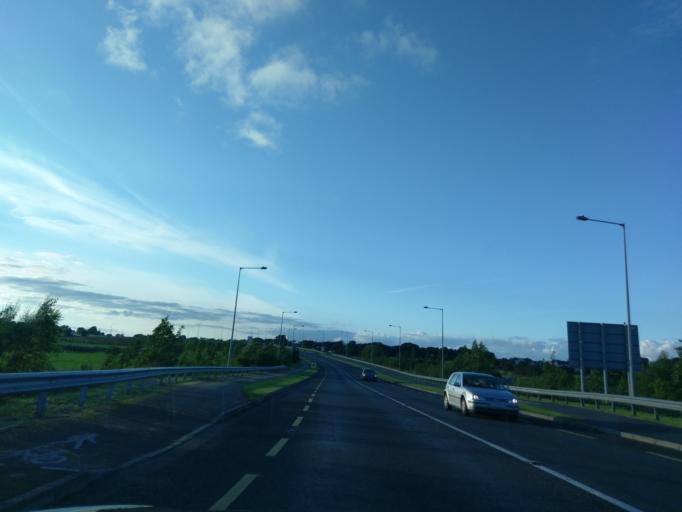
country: IE
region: Connaught
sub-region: County Galway
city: Athenry
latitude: 53.2905
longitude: -8.7564
